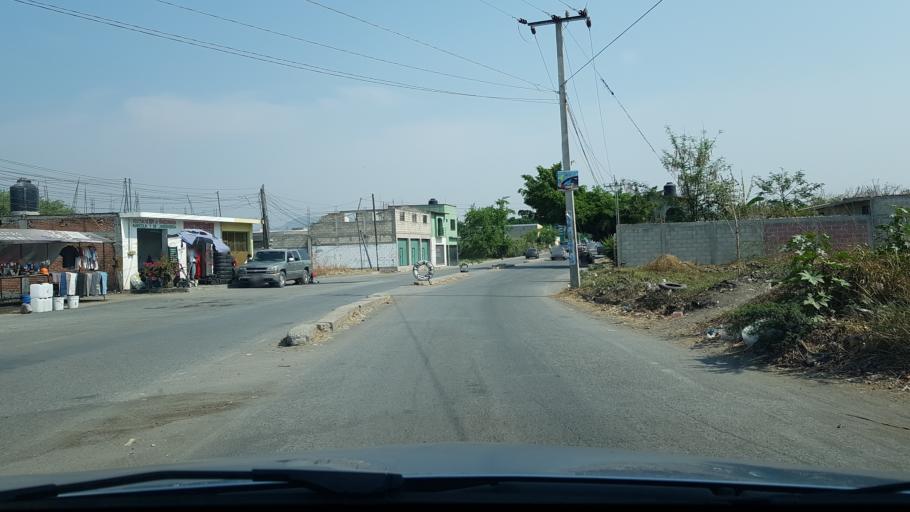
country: MX
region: Morelos
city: Zacatepec
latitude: 18.6653
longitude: -99.1863
